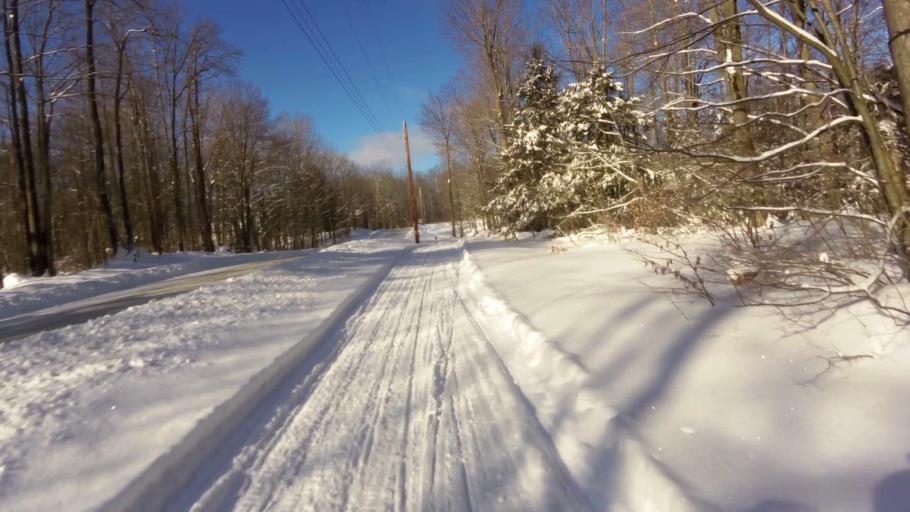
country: US
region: New York
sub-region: Chautauqua County
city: Falconer
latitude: 42.2605
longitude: -79.1186
